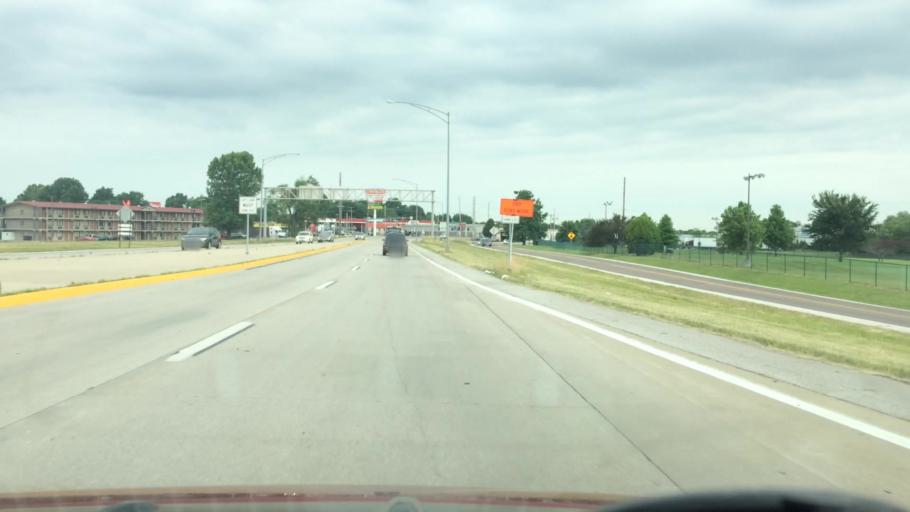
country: US
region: Missouri
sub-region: Greene County
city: Springfield
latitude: 37.2519
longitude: -93.2634
